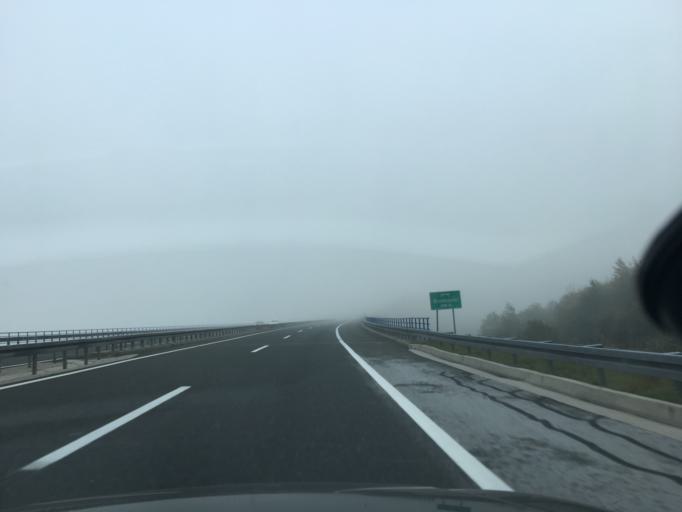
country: HR
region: Licko-Senjska
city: Otocac
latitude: 44.9058
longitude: 15.1778
